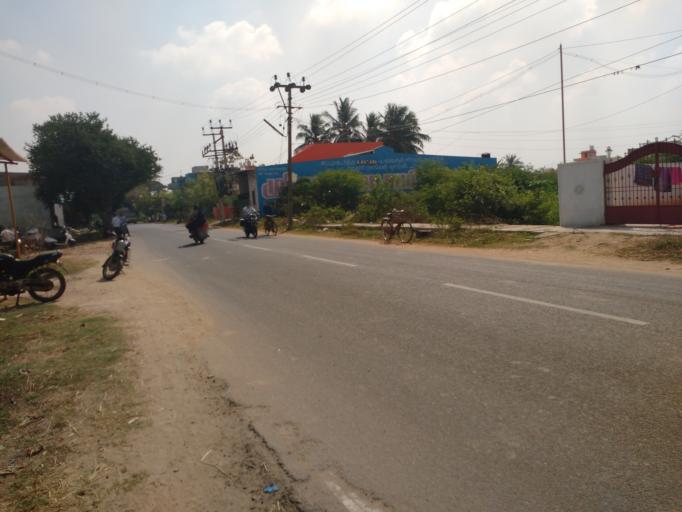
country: IN
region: Pondicherry
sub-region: Puducherry
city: Puducherry
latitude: 11.9100
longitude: 79.7645
